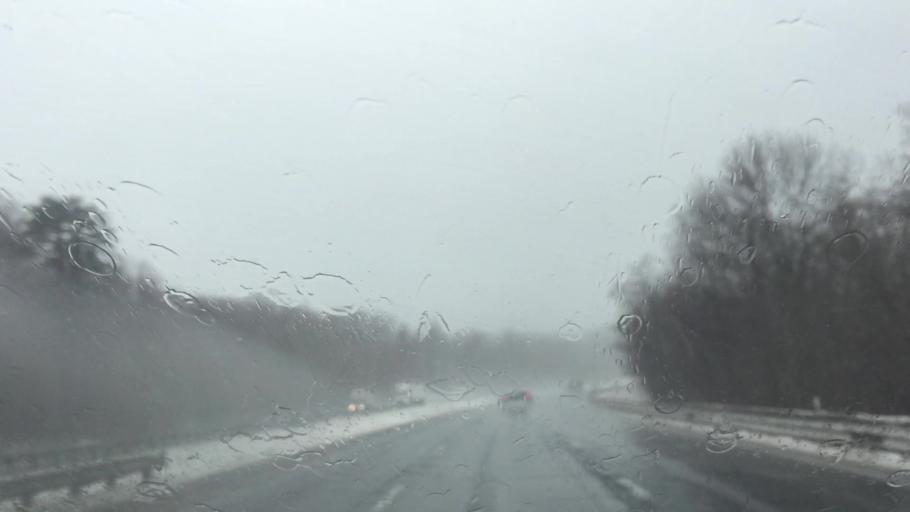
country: US
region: Massachusetts
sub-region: Hampden County
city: Granville
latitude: 42.1727
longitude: -72.9069
